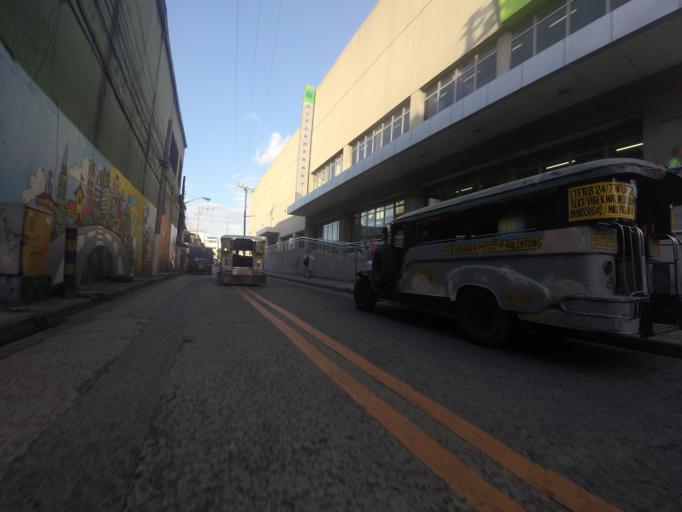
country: PH
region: Metro Manila
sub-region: San Juan
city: San Juan
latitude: 14.5926
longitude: 121.0295
